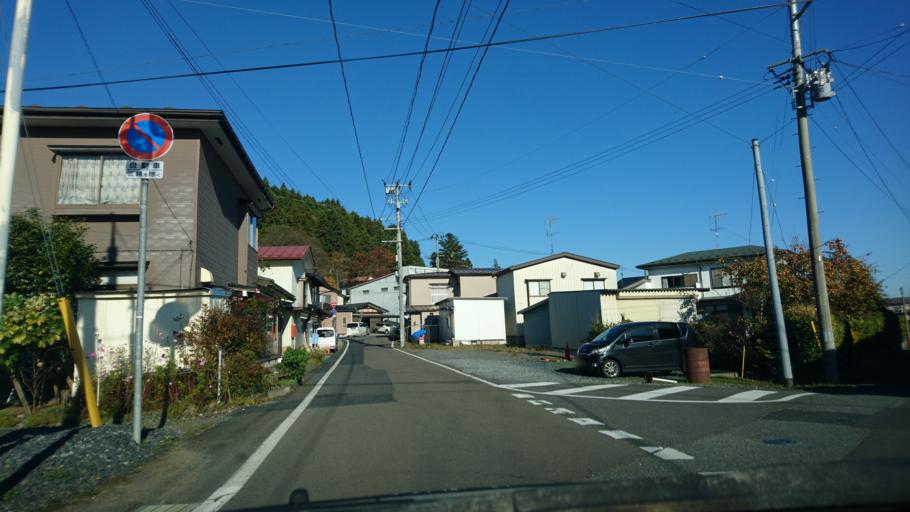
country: JP
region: Iwate
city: Mizusawa
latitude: 39.0422
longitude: 141.1207
